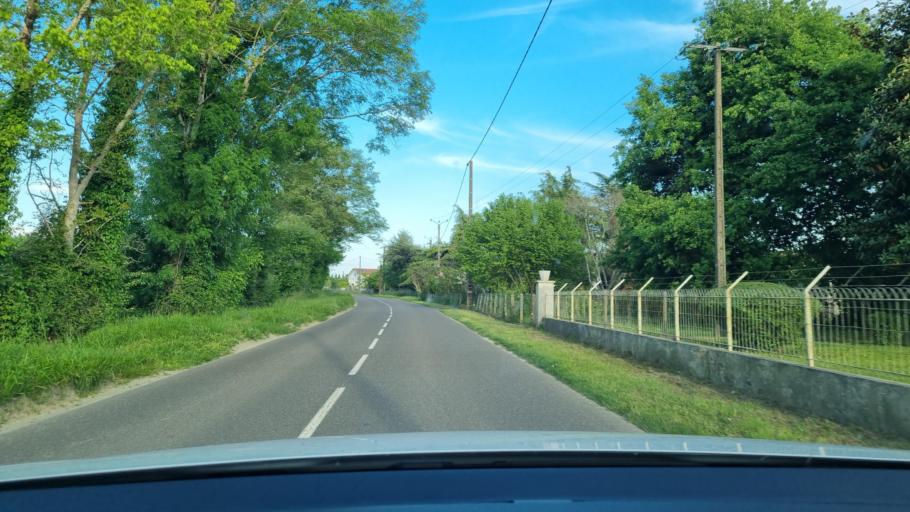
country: FR
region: Aquitaine
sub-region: Departement des Landes
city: Peyrehorade
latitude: 43.5398
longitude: -1.1240
